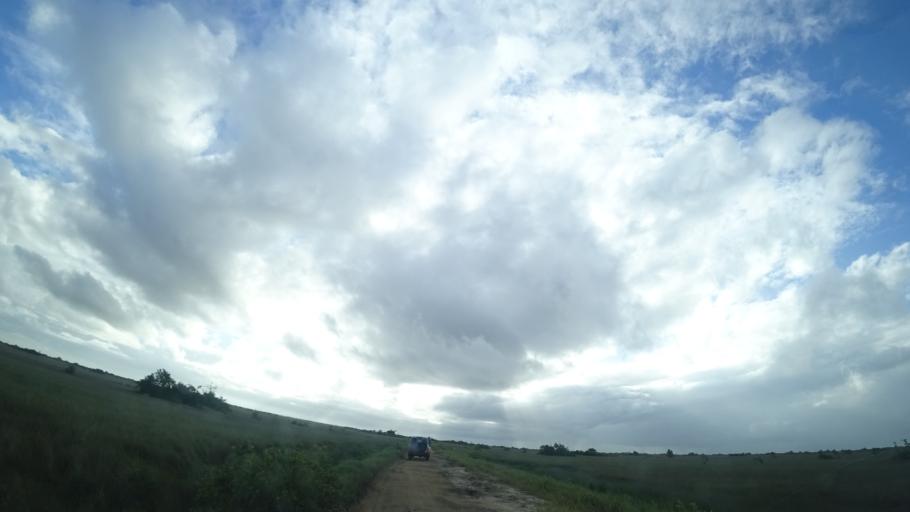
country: MZ
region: Sofala
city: Beira
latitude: -19.7047
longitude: 35.0206
